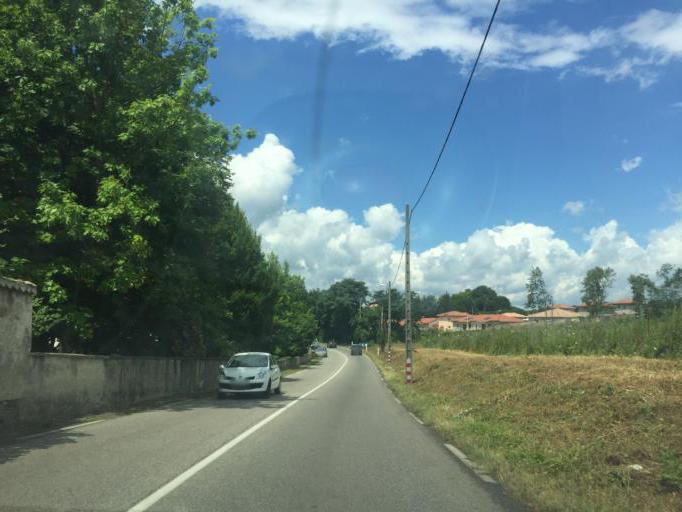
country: FR
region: Rhone-Alpes
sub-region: Departement de l'Isere
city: Charvieu-Chavagneux
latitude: 45.7510
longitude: 5.1562
